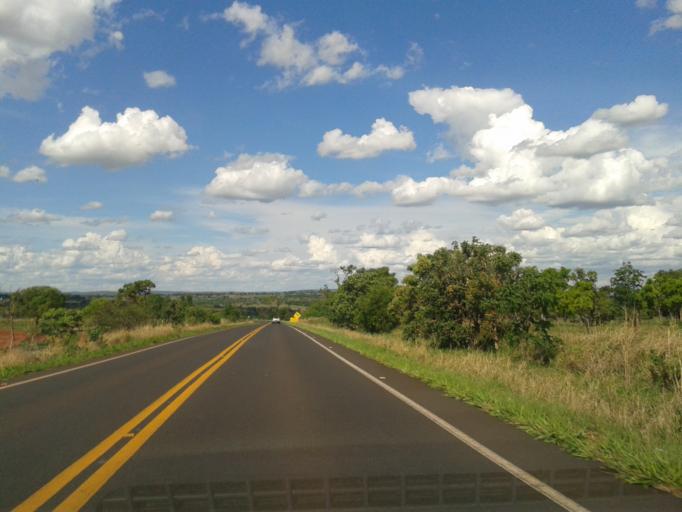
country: BR
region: Minas Gerais
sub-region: Iturama
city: Iturama
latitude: -19.5927
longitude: -50.0370
